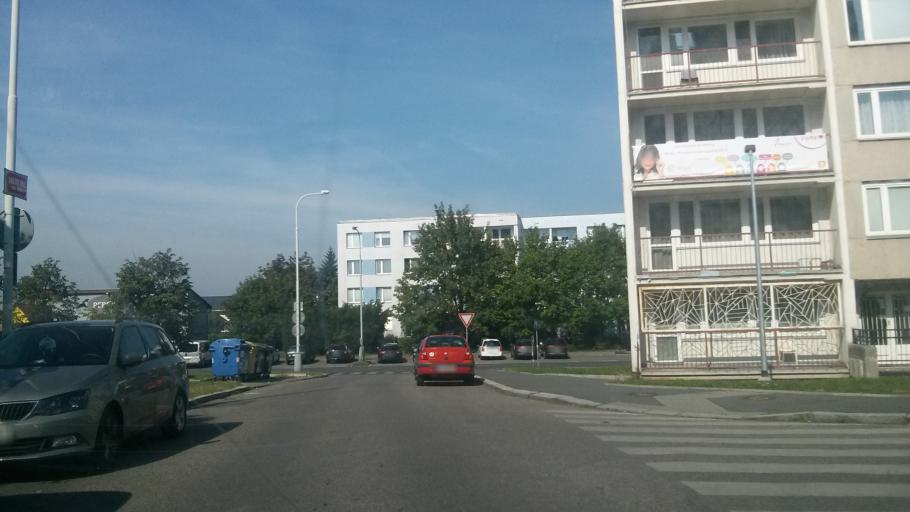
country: CZ
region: Central Bohemia
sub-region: Okres Praha-Zapad
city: Pruhonice
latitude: 50.0327
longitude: 14.5258
